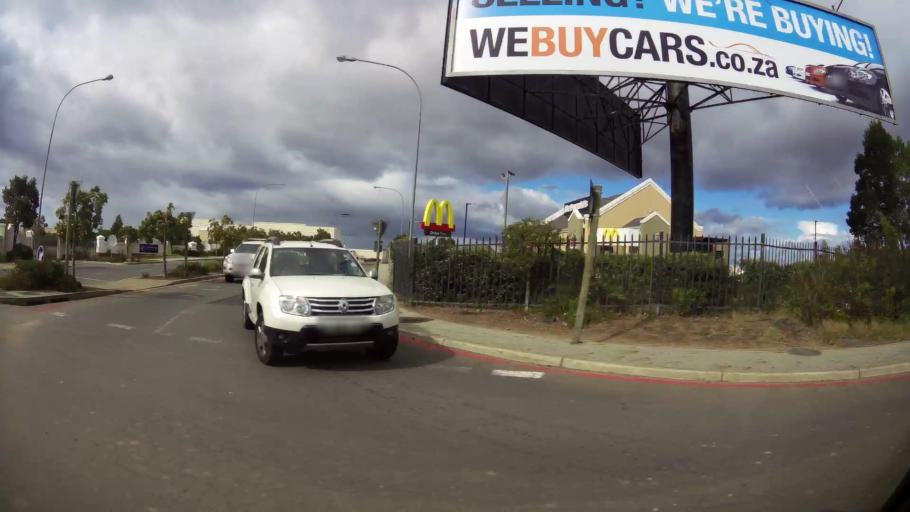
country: ZA
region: Western Cape
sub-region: Eden District Municipality
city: George
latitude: -33.9854
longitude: 22.5016
